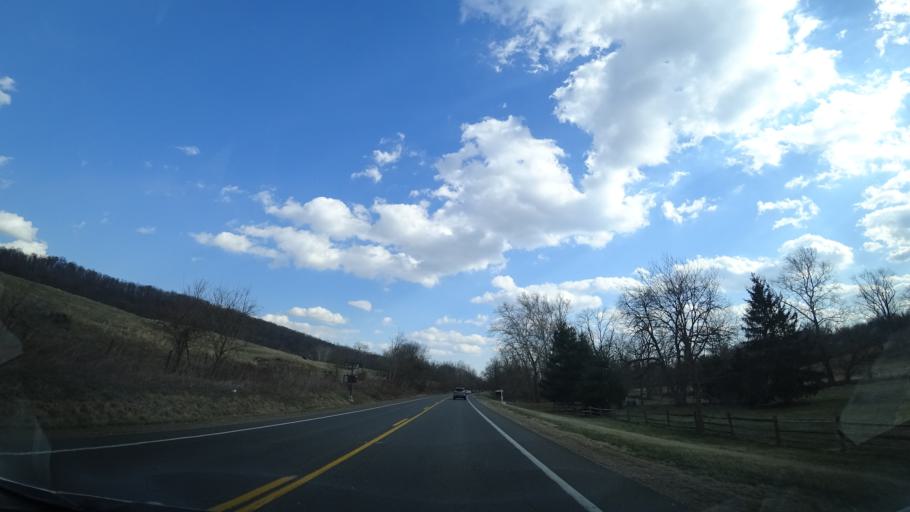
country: US
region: Virginia
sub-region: Fauquier County
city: Marshall
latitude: 38.9596
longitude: -77.9441
